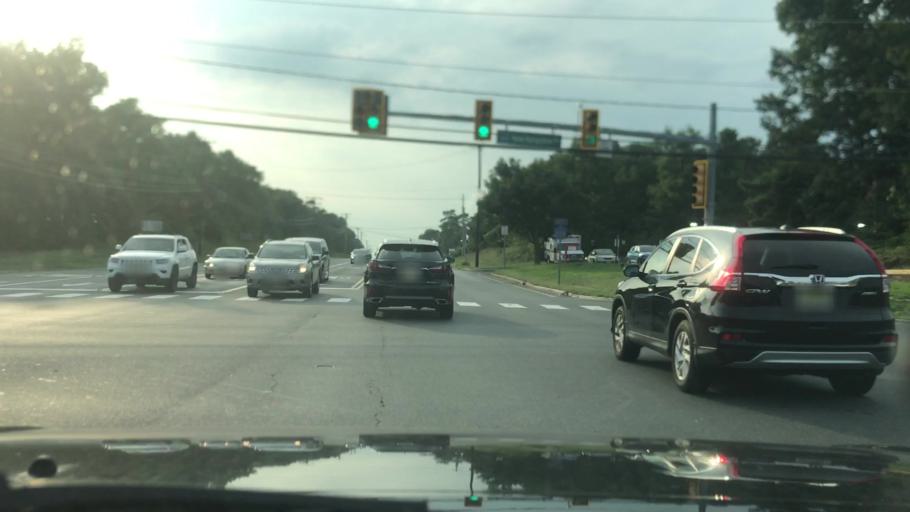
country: US
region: New Jersey
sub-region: Ocean County
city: Leisure Village
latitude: 40.0758
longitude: -74.1843
